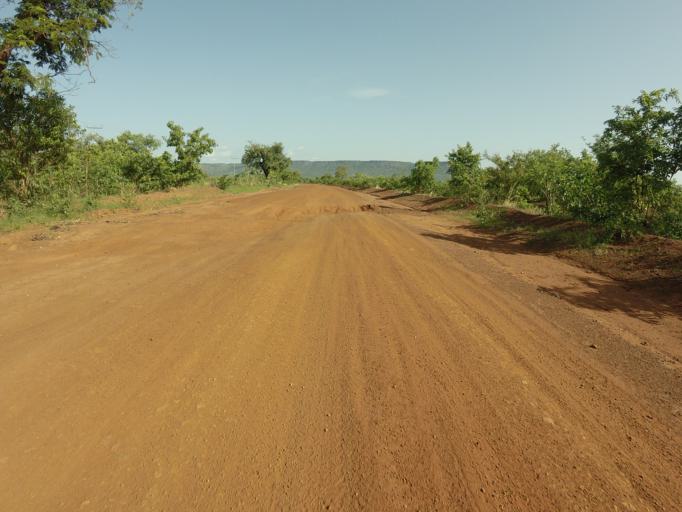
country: GH
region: Upper East
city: Bawku
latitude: 10.6865
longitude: -0.2157
